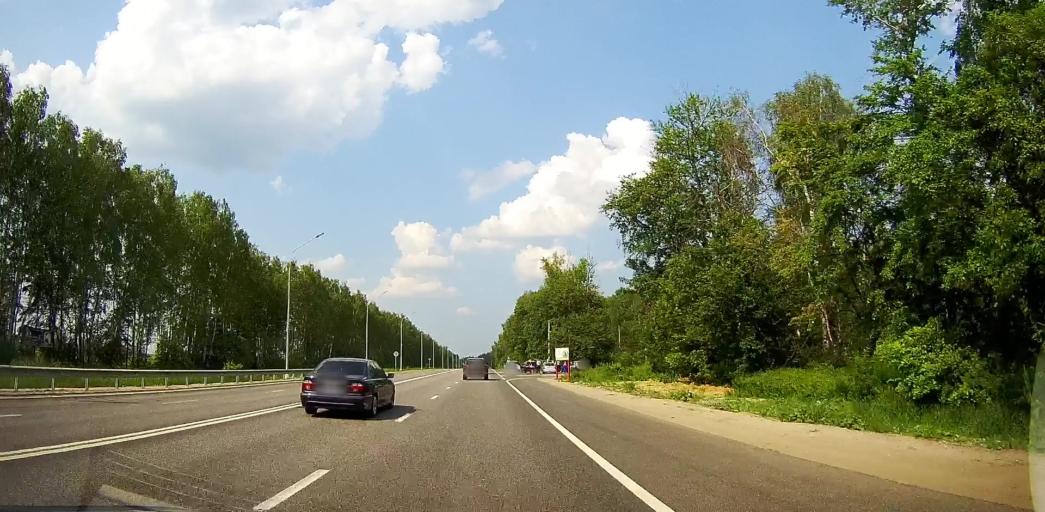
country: RU
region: Moskovskaya
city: Mikhnevo
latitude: 55.0817
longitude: 37.9535
